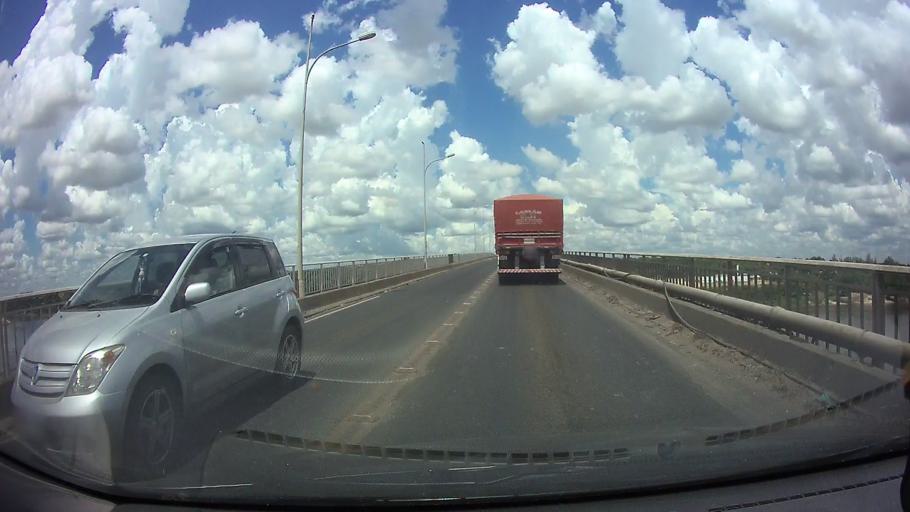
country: PY
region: Central
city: Colonia Mariano Roque Alonso
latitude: -25.1832
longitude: -57.5476
